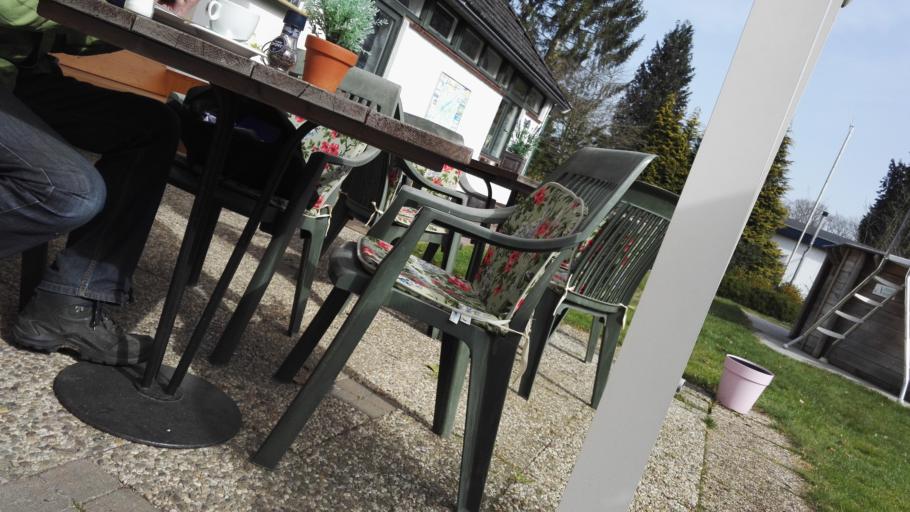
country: NL
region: Gelderland
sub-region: Gemeente Epe
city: Epe
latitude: 52.3522
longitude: 5.9622
